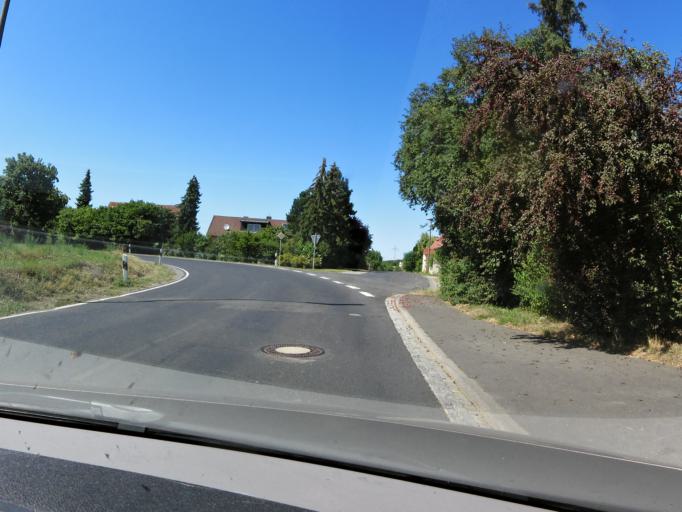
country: DE
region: Bavaria
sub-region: Regierungsbezirk Unterfranken
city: Biebelried
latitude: 49.7313
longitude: 10.0877
